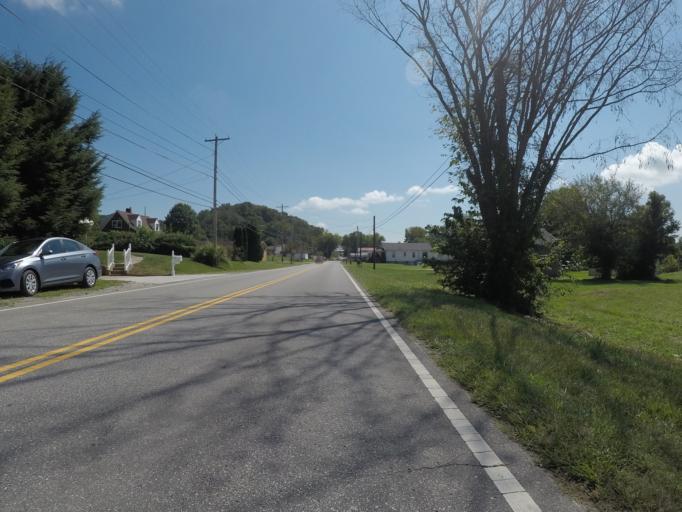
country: US
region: West Virginia
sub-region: Wayne County
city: Kenova
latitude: 38.4106
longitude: -82.5760
